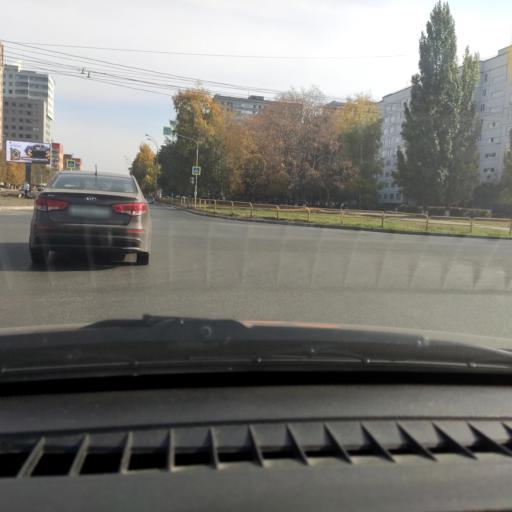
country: RU
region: Samara
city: Tol'yatti
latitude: 53.5135
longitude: 49.2934
